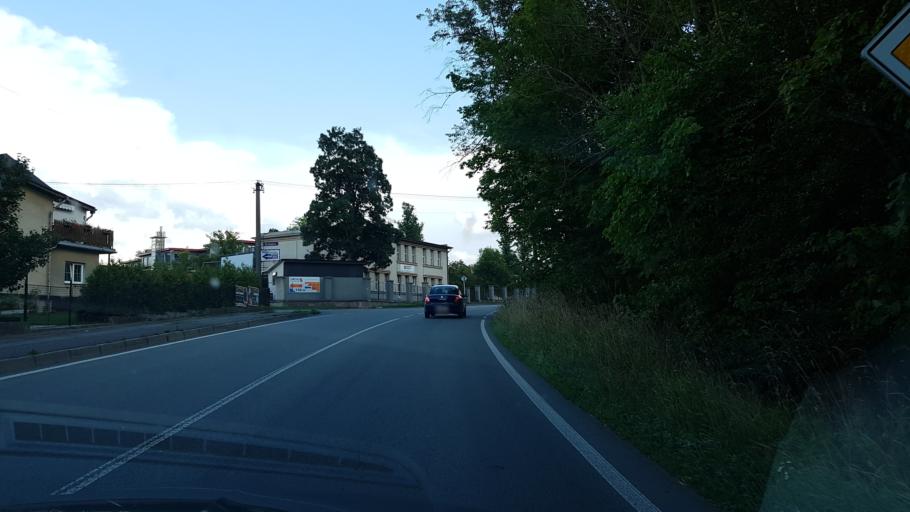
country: CZ
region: Pardubicky
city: Zamberk
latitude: 50.0928
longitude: 16.4522
